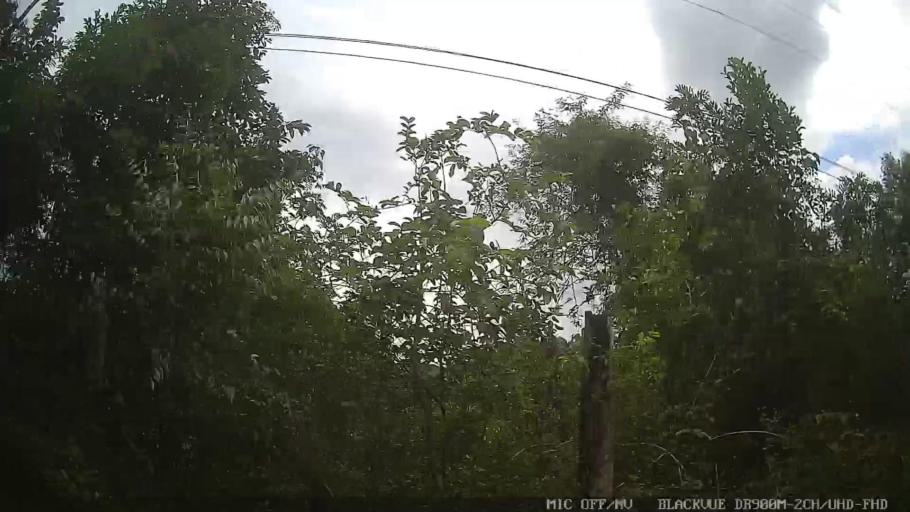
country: BR
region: Sao Paulo
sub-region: Santa Isabel
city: Santa Isabel
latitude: -23.3945
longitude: -46.2394
